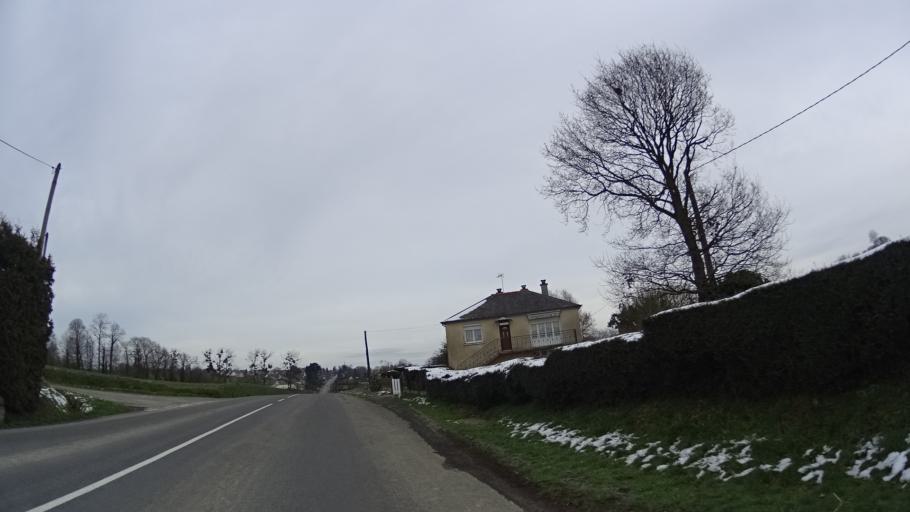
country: FR
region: Brittany
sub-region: Departement d'Ille-et-Vilaine
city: Irodouer
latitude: 48.2437
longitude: -2.0047
